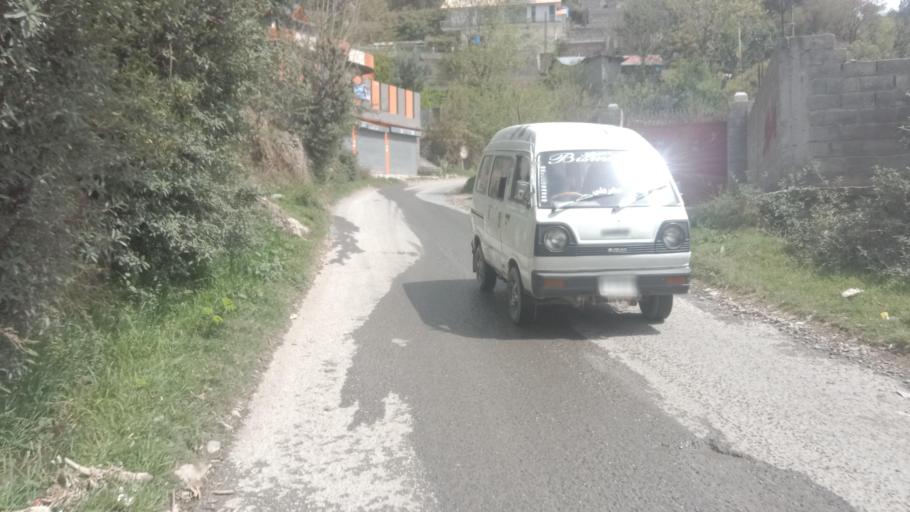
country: PK
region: Khyber Pakhtunkhwa
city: Abbottabad
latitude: 34.1684
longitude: 73.2814
